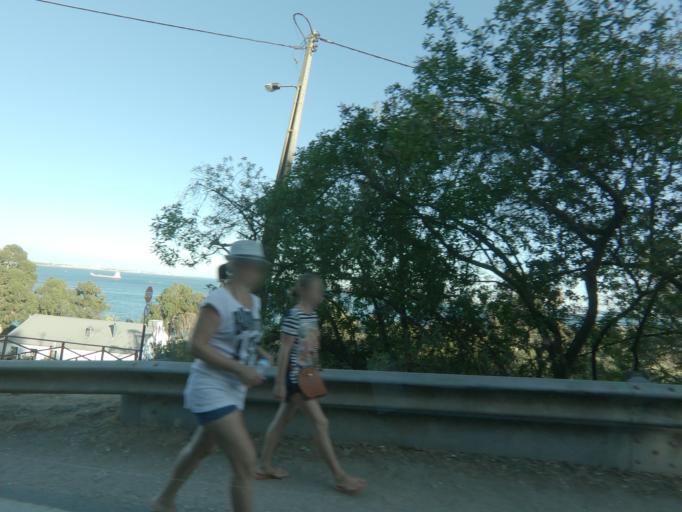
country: PT
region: Setubal
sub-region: Setubal
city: Setubal
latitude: 38.5130
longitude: -8.9125
